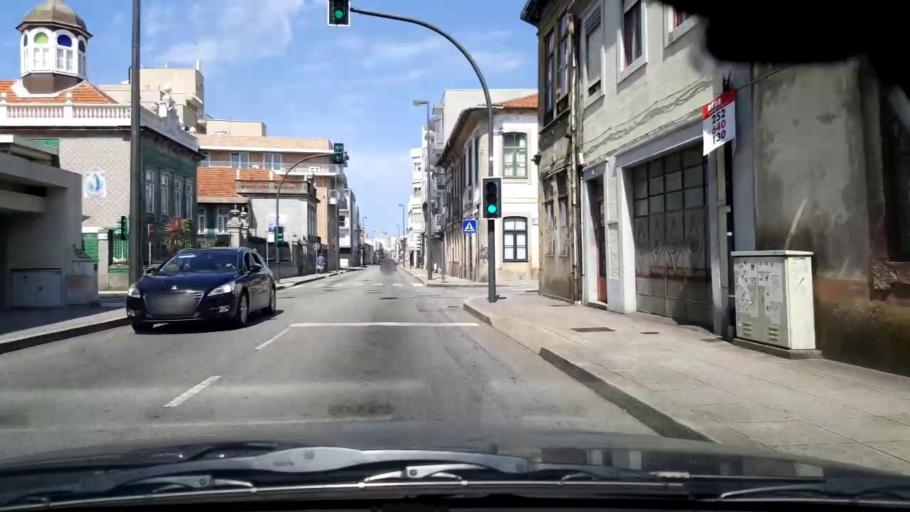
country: PT
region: Porto
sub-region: Povoa de Varzim
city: Povoa de Varzim
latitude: 41.3749
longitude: -8.7565
